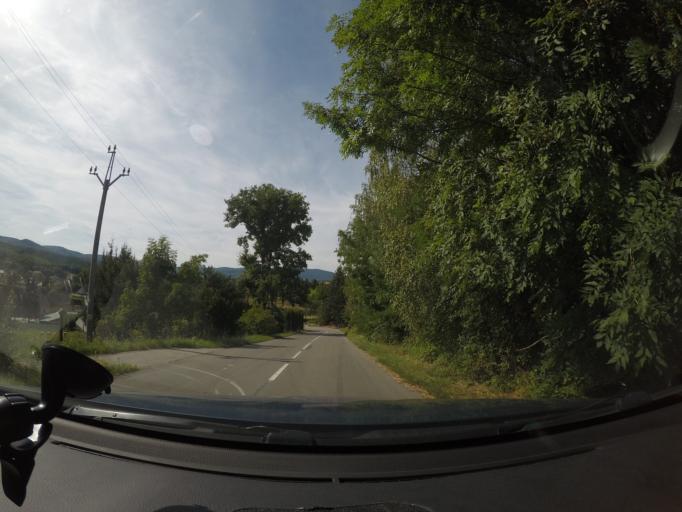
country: SK
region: Nitriansky
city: Banovce nad Bebravou
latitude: 48.7112
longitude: 18.1256
